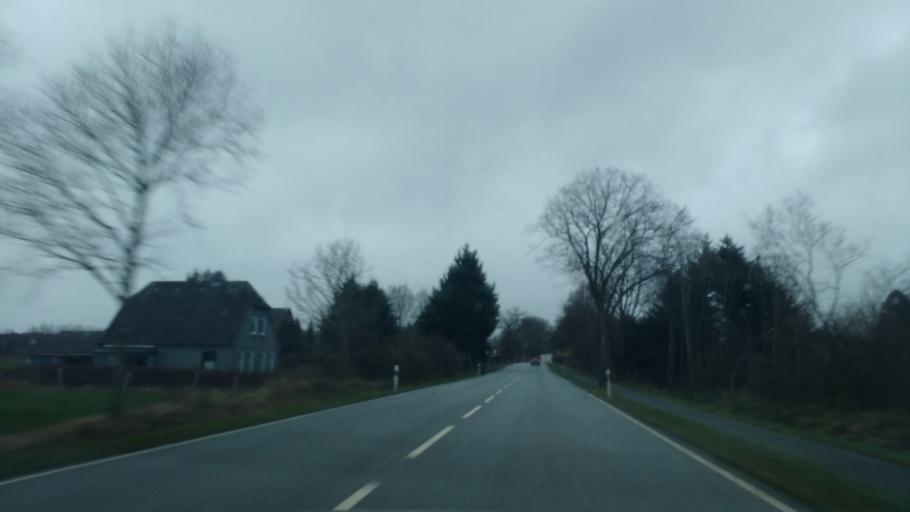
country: DE
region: Schleswig-Holstein
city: Jahrsdorf
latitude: 54.0537
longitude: 9.6299
